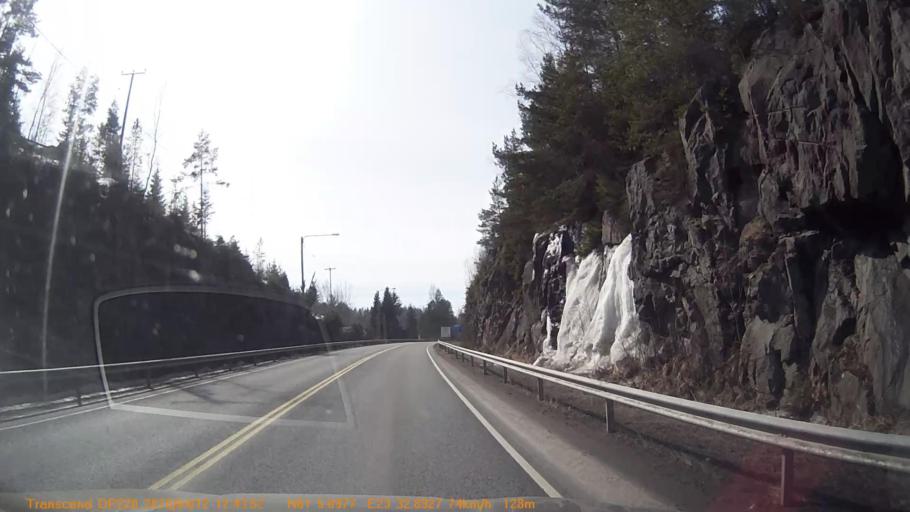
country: FI
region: Pirkanmaa
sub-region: Etelae-Pirkanmaa
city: Urjala
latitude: 61.0848
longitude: 23.5479
